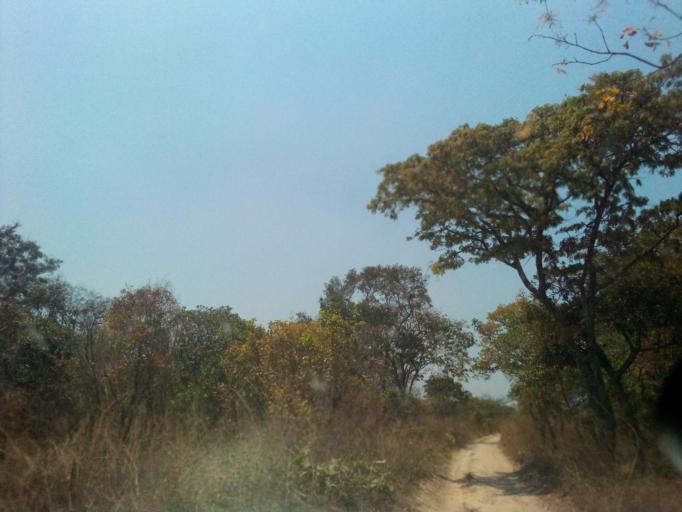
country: ZM
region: Copperbelt
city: Kataba
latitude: -12.2490
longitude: 30.3927
